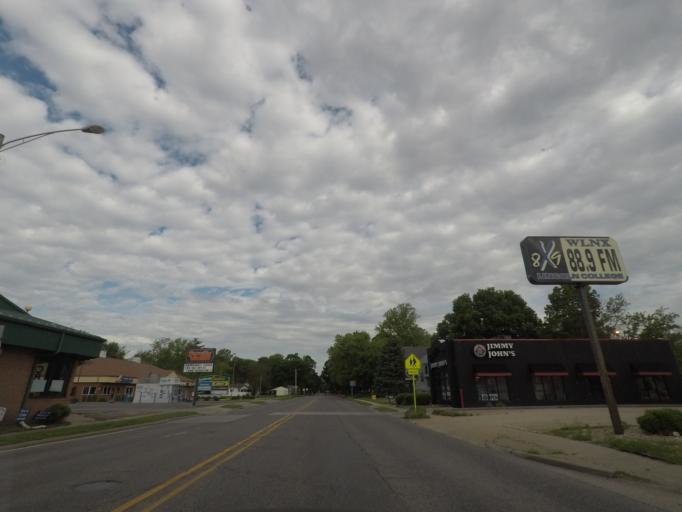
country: US
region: Illinois
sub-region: Logan County
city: Lincoln
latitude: 40.1540
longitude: -89.3608
